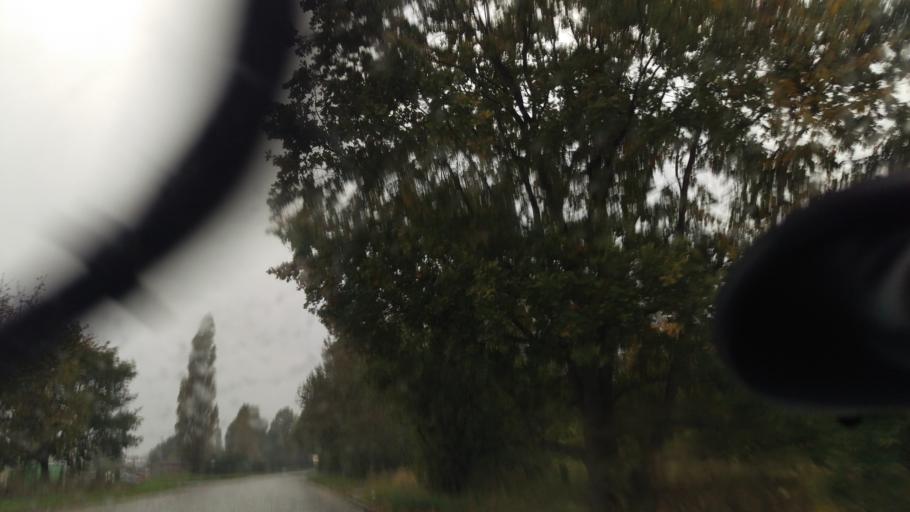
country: PL
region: West Pomeranian Voivodeship
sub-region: Szczecin
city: Szczecin
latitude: 53.3873
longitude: 14.6473
